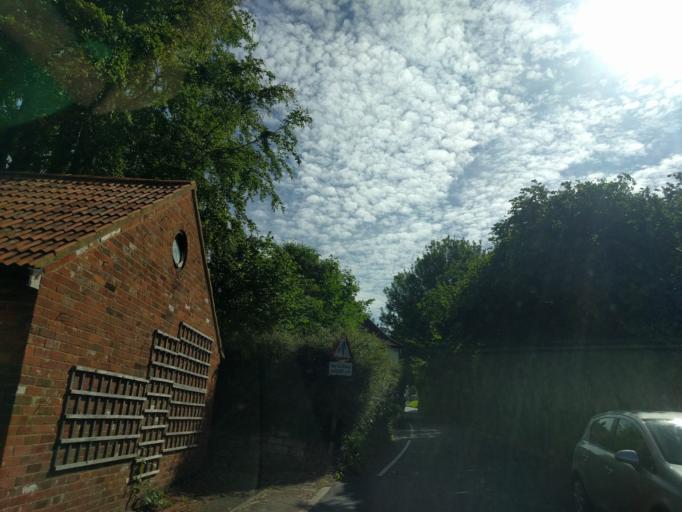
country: GB
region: England
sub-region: Wiltshire
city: Edington
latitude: 51.2770
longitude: -2.1057
